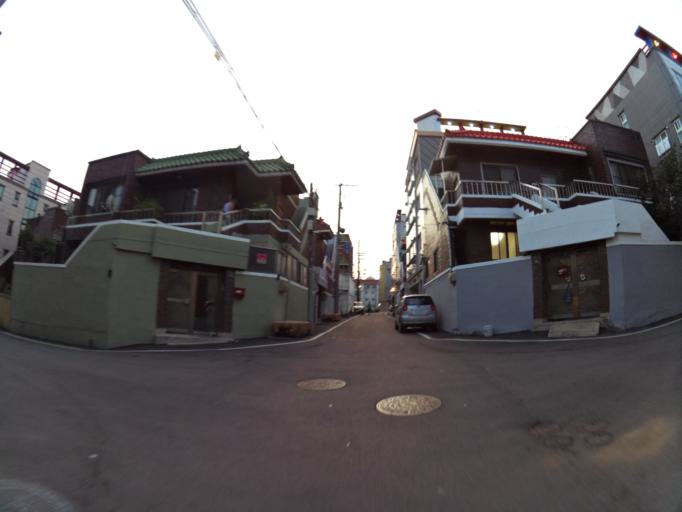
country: KR
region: Gyeongsangbuk-do
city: Gyeongsan-si
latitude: 35.8404
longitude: 128.7563
